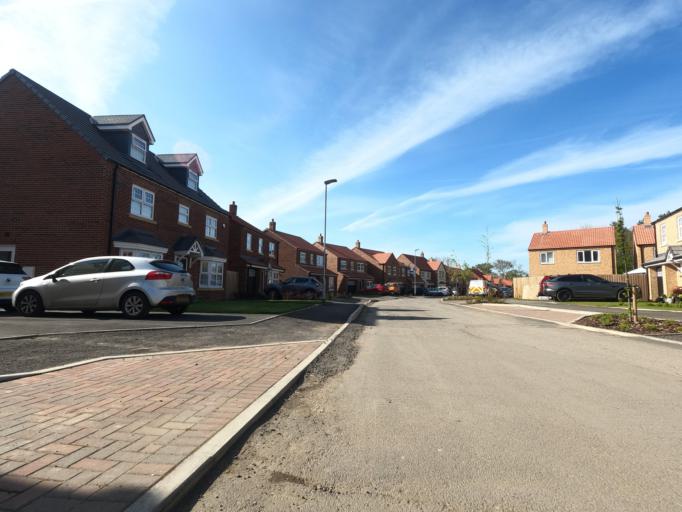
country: GB
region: England
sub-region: Northumberland
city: Hebron
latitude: 55.1871
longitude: -1.7112
